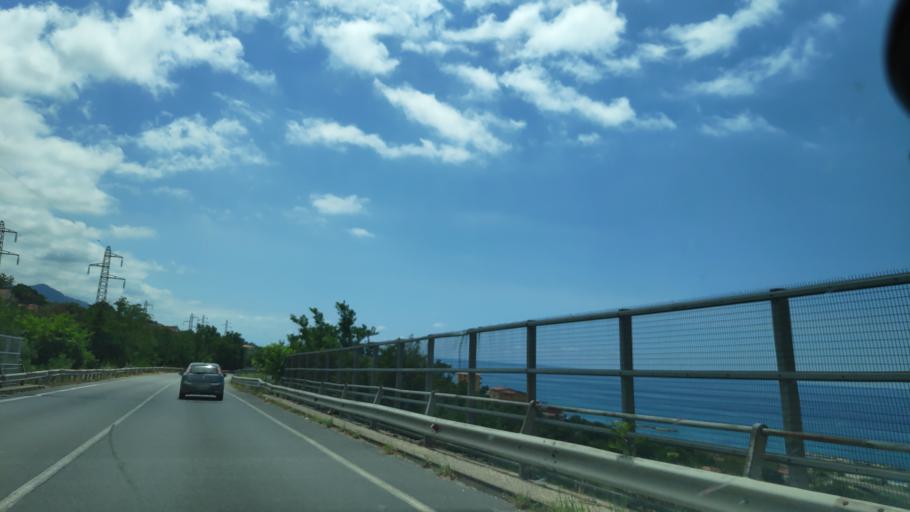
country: IT
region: Calabria
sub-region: Provincia di Cosenza
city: Paola
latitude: 39.3454
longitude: 16.0446
